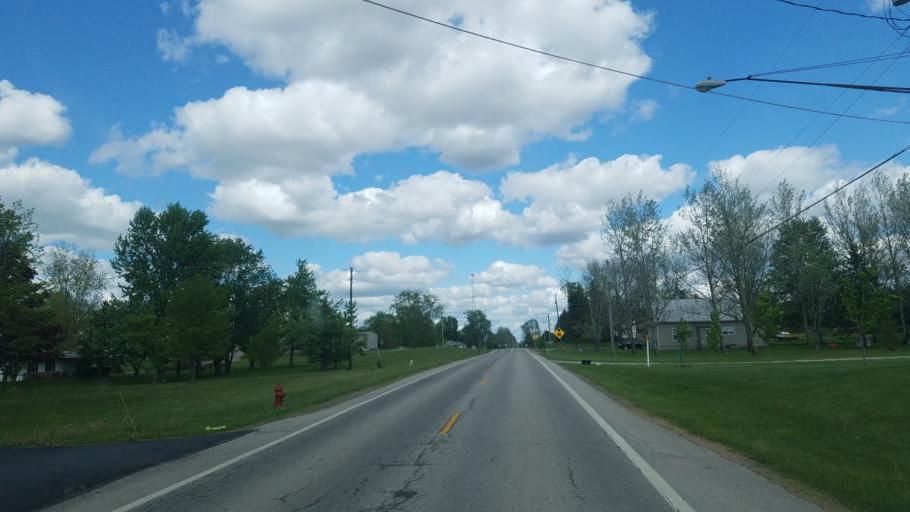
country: US
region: Ohio
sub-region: Morrow County
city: Cardington
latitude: 40.5061
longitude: -82.9004
